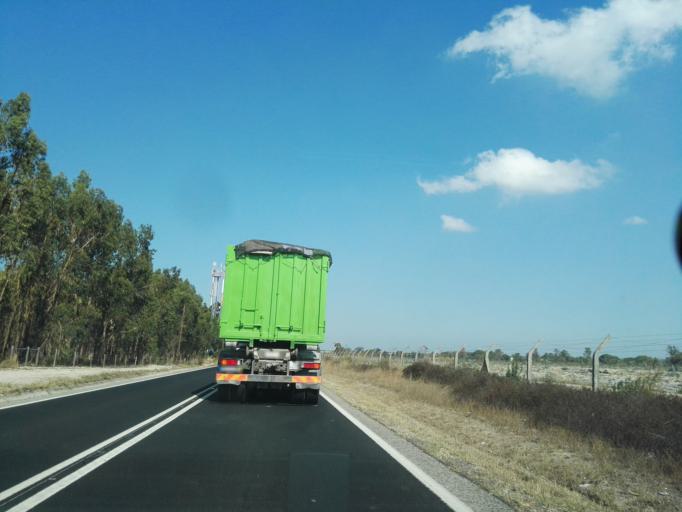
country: PT
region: Setubal
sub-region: Alcochete
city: Alcochete
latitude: 38.7801
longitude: -8.8830
